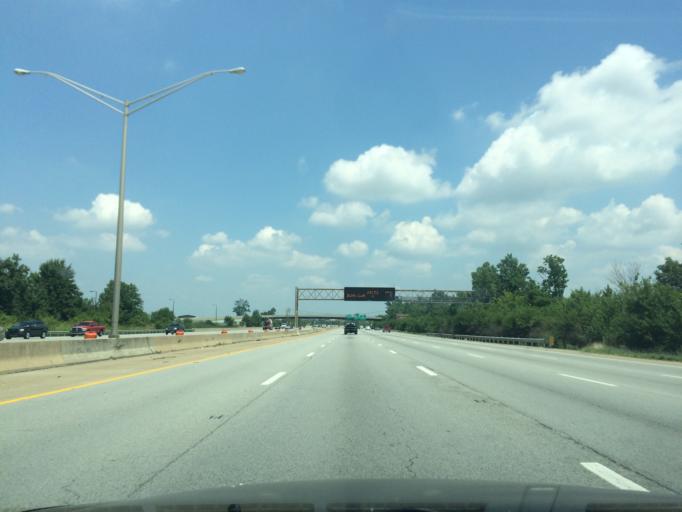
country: US
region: Kentucky
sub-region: Jefferson County
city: Audubon Park
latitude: 38.1645
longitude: -85.7208
